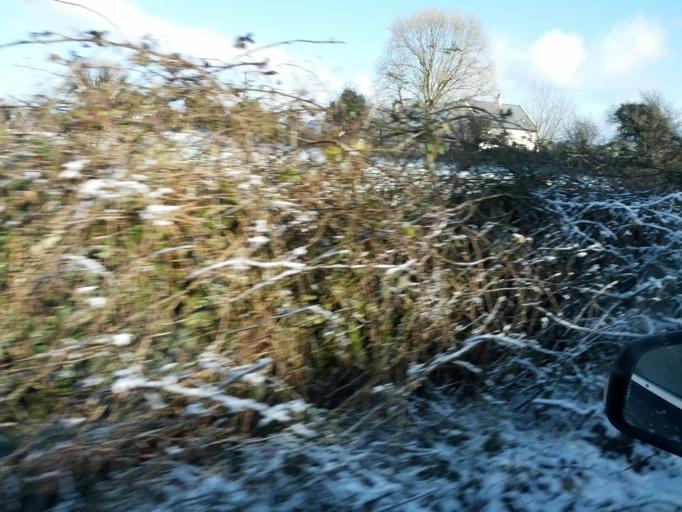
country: IE
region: Connaught
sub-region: County Galway
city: Athenry
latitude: 53.1847
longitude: -8.7862
